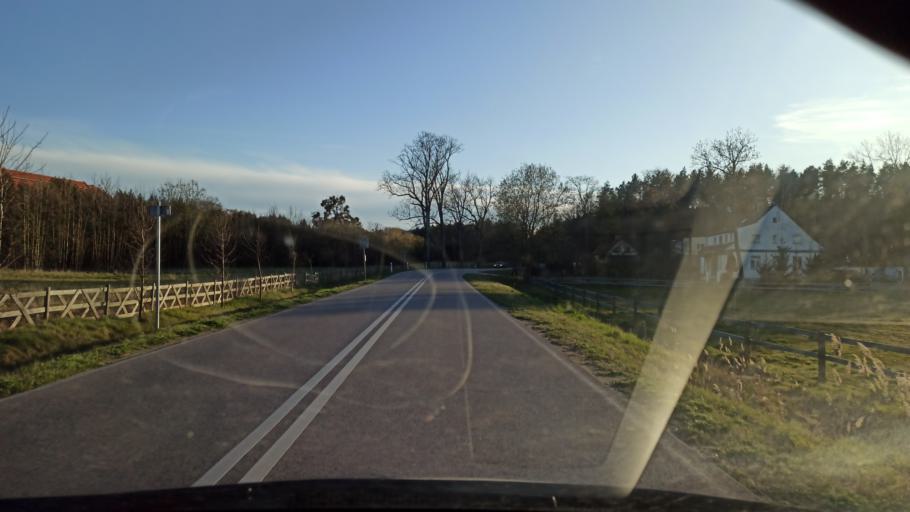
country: PL
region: Warmian-Masurian Voivodeship
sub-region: Powiat elblaski
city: Tolkmicko
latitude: 54.3040
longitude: 19.5079
